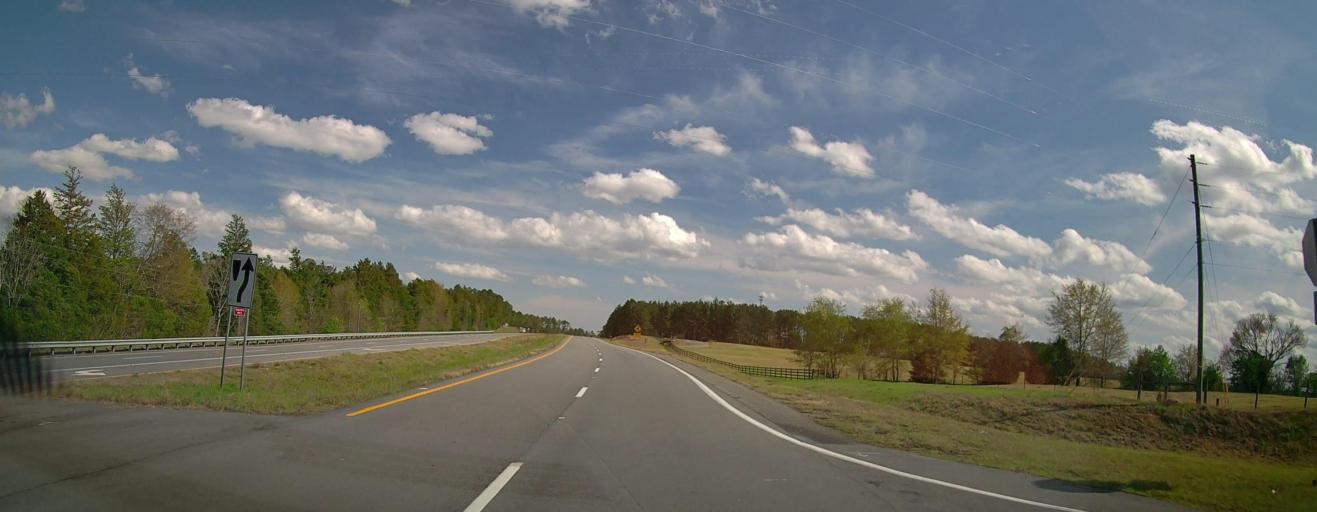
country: US
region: Georgia
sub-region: Baldwin County
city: Hardwick
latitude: 33.0022
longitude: -83.2199
